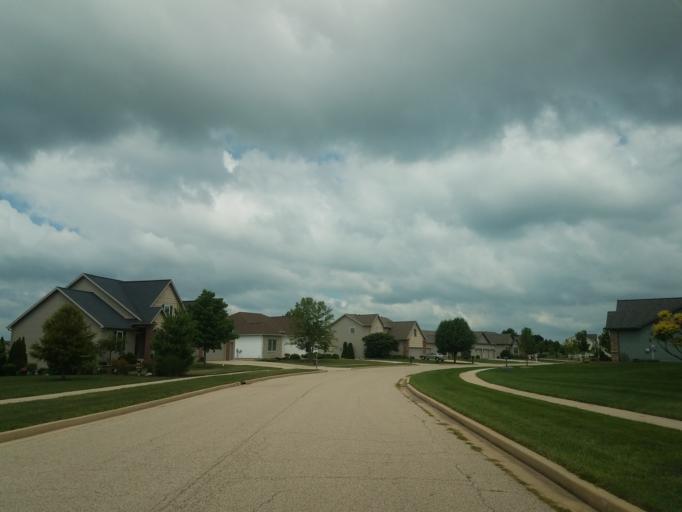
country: US
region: Illinois
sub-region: McLean County
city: Bloomington
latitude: 40.4425
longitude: -89.0377
